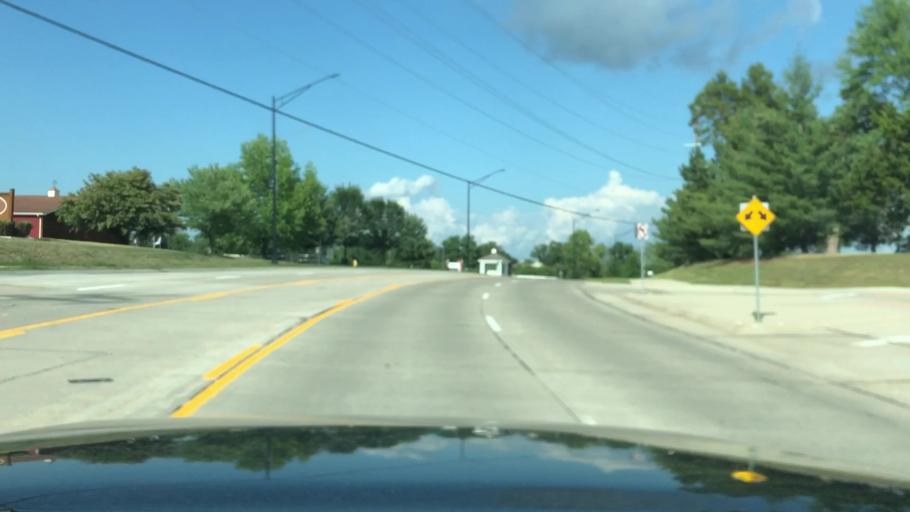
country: US
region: Missouri
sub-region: Saint Charles County
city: Wentzville
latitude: 38.8246
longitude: -90.8764
